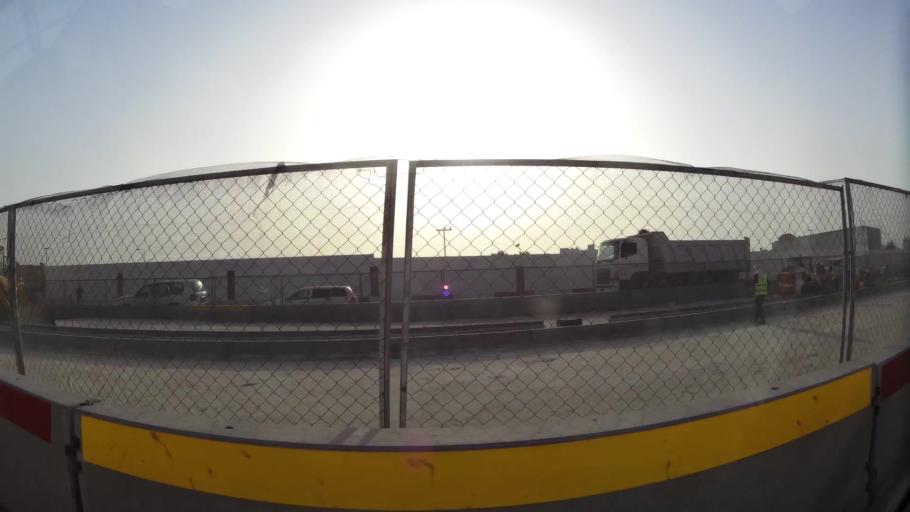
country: QA
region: Baladiyat ar Rayyan
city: Ar Rayyan
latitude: 25.2458
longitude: 51.4536
